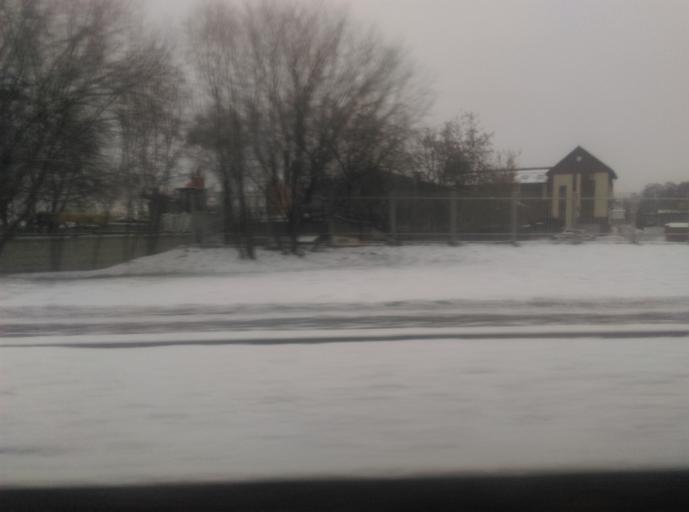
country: RU
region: Moskovskaya
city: Bol'shaya Setun'
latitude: 55.7083
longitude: 37.4218
